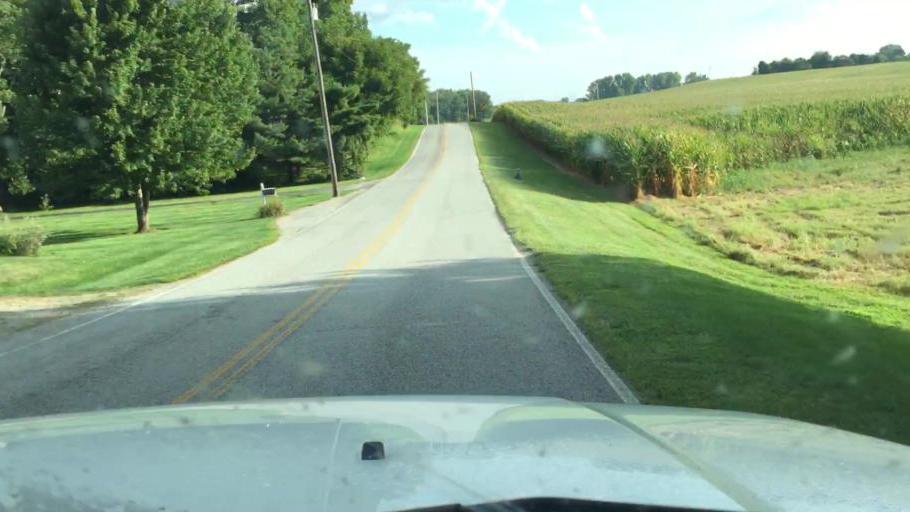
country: US
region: Ohio
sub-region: Champaign County
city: Mechanicsburg
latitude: 40.0616
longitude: -83.5892
